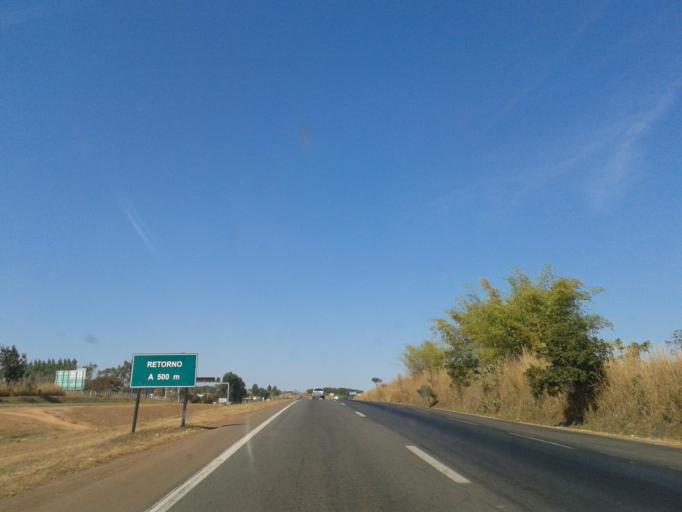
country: BR
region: Goias
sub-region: Aparecida De Goiania
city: Aparecida de Goiania
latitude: -16.8824
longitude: -49.2535
